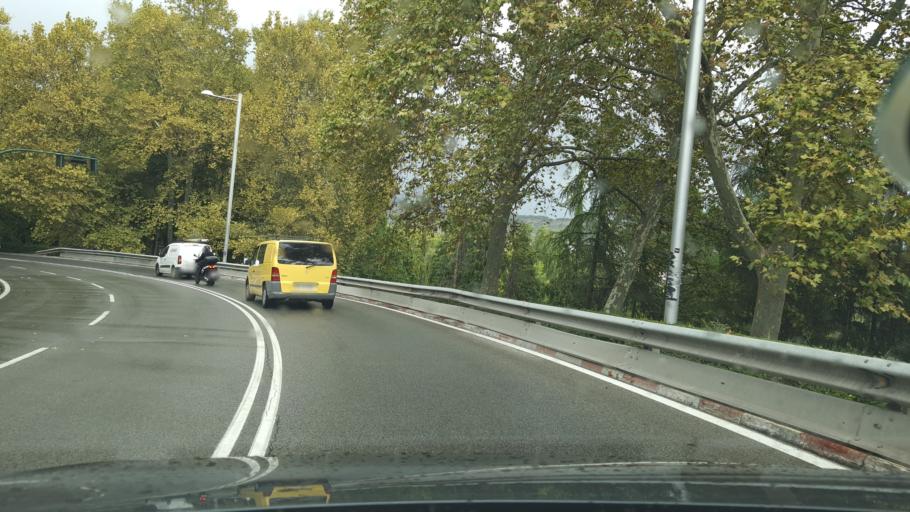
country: ES
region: Navarre
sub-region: Provincia de Navarra
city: Pamplona
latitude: 42.8177
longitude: -1.6377
